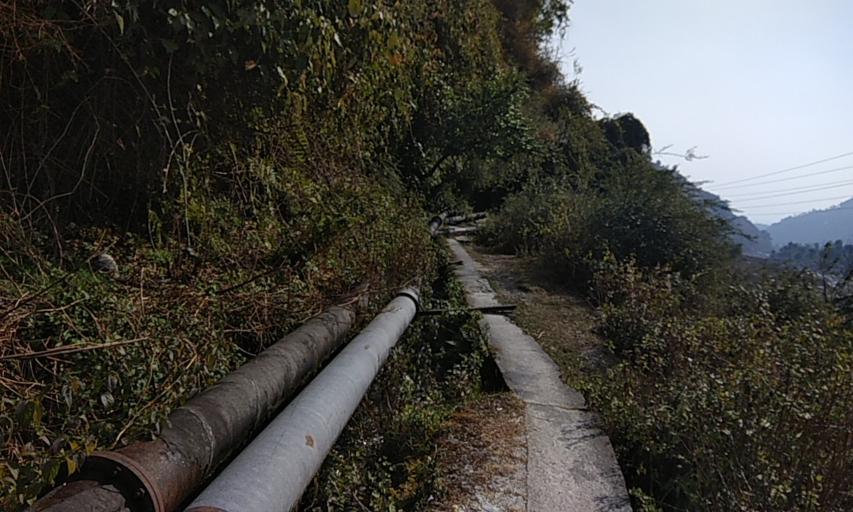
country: IN
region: Himachal Pradesh
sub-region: Kangra
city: Palampur
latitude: 32.1533
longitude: 76.5438
